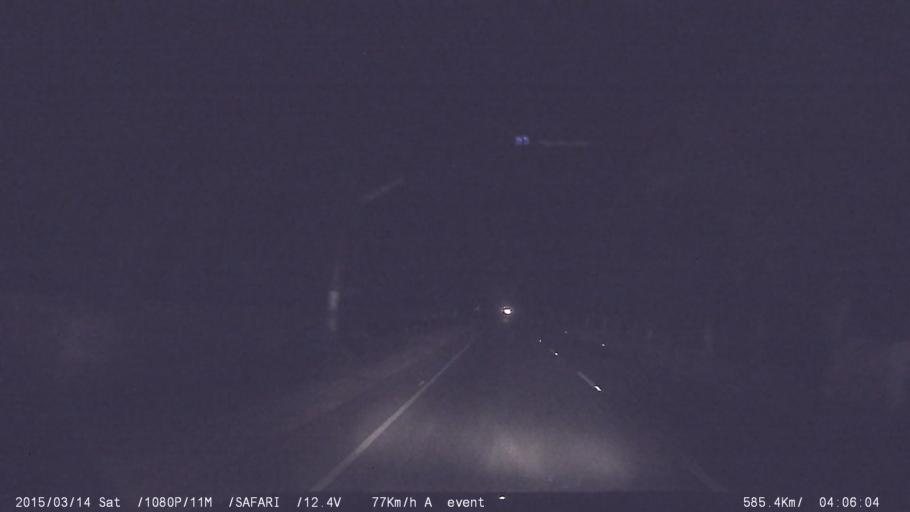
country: IN
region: Kerala
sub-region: Alappuzha
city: Alleppey
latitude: 9.4403
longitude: 76.4107
